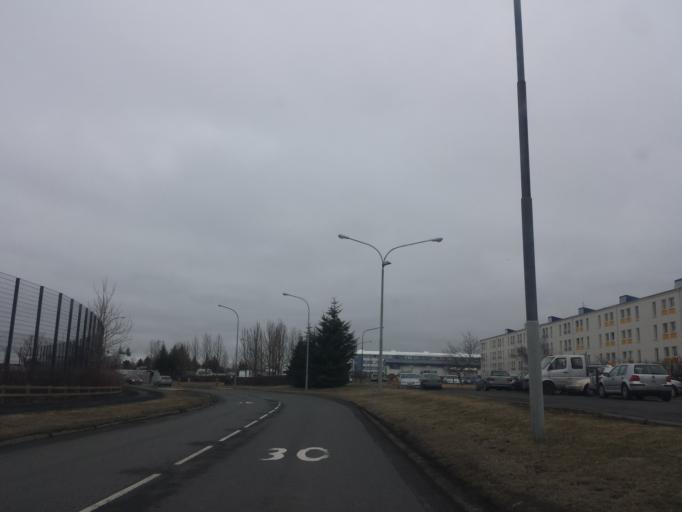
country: IS
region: Capital Region
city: Reykjavik
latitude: 64.1017
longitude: -21.8194
